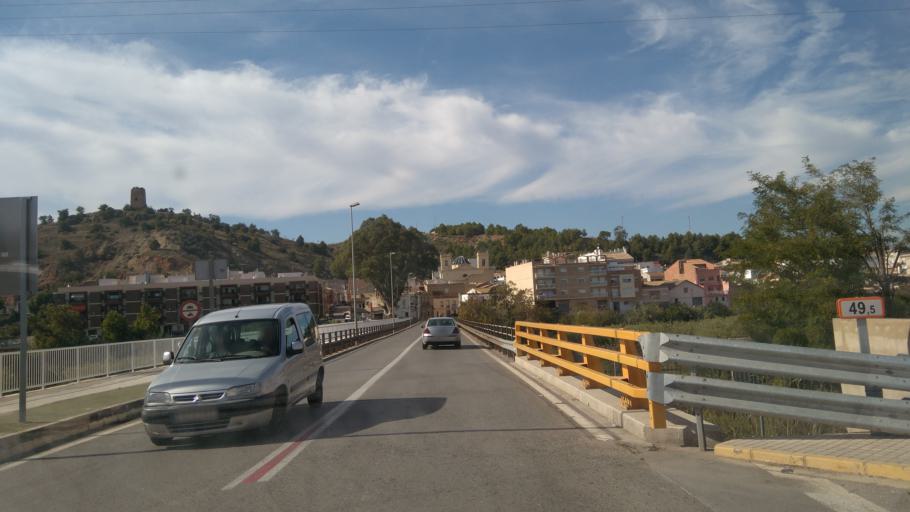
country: ES
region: Valencia
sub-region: Provincia de Valencia
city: Montroy
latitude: 39.3370
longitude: -0.6109
